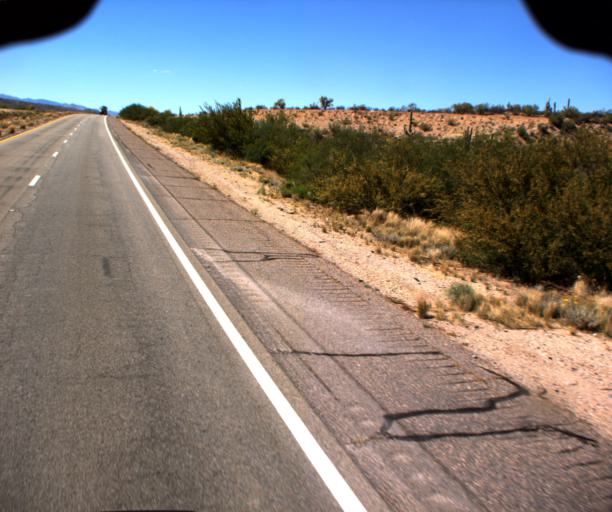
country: US
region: Arizona
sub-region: Yavapai County
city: Bagdad
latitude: 34.6452
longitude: -113.5676
